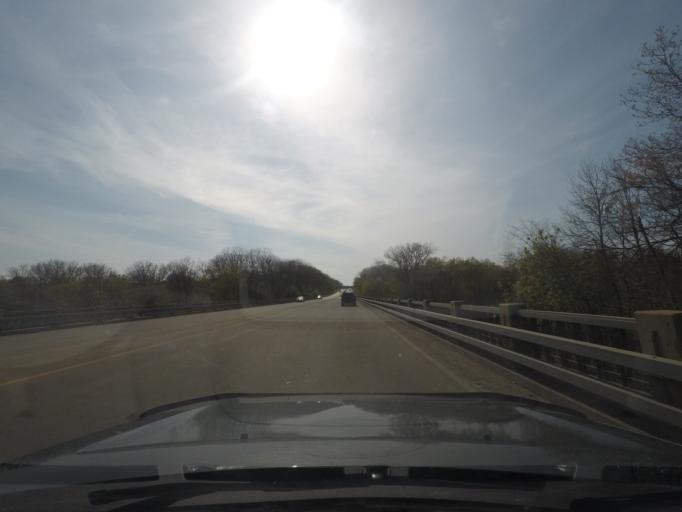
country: US
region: Michigan
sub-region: Berrien County
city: Niles
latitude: 41.8013
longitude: -86.2664
